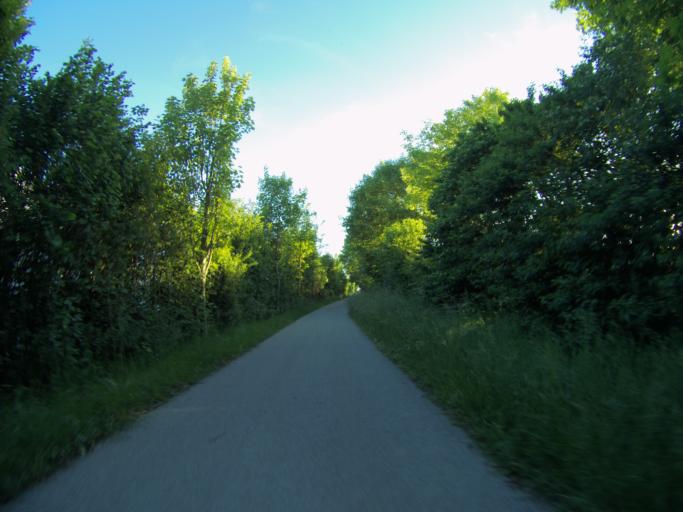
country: DE
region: Bavaria
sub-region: Upper Bavaria
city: Langenbach
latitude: 48.4357
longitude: 11.8640
